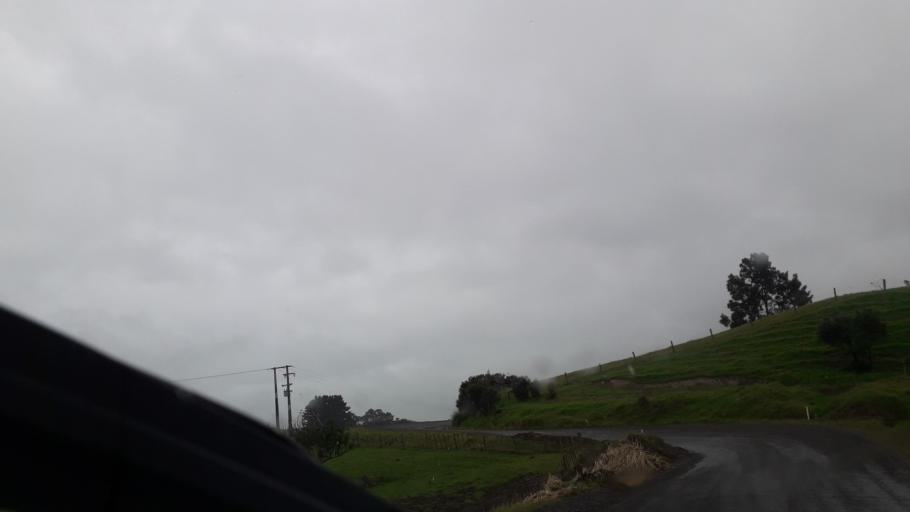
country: NZ
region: Northland
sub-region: Far North District
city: Kaitaia
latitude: -35.4098
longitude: 173.3648
